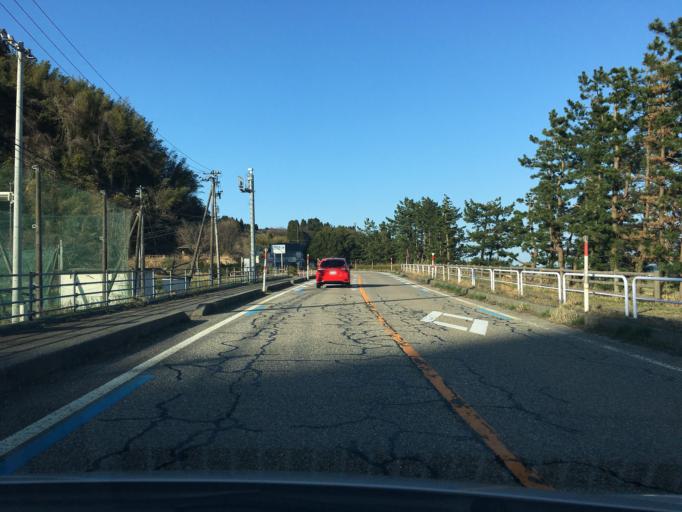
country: JP
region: Toyama
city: Himi
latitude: 36.9190
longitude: 137.0263
